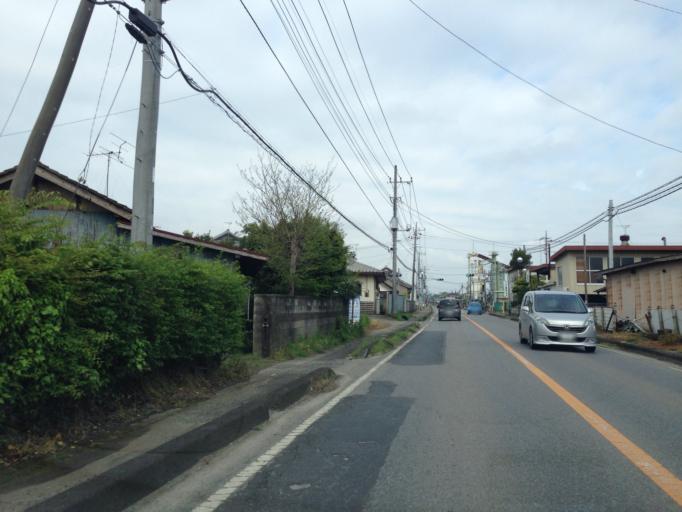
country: JP
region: Ibaraki
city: Ishige
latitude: 36.1530
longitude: 139.9802
